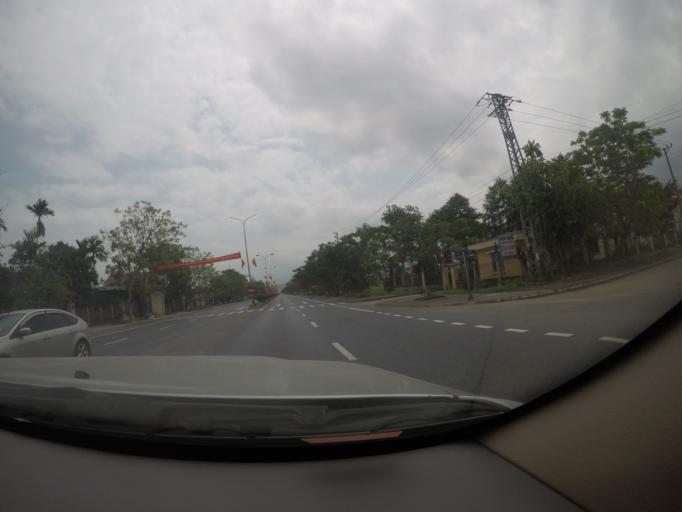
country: VN
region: Thua Thien-Hue
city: Phu Loc
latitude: 16.2746
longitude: 107.8661
